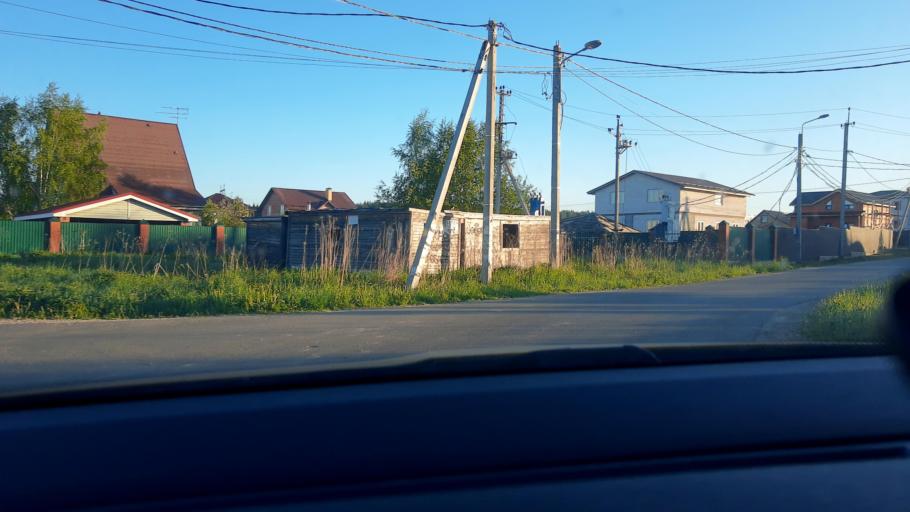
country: RU
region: Moskovskaya
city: Selyatino
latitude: 55.5002
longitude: 36.9233
